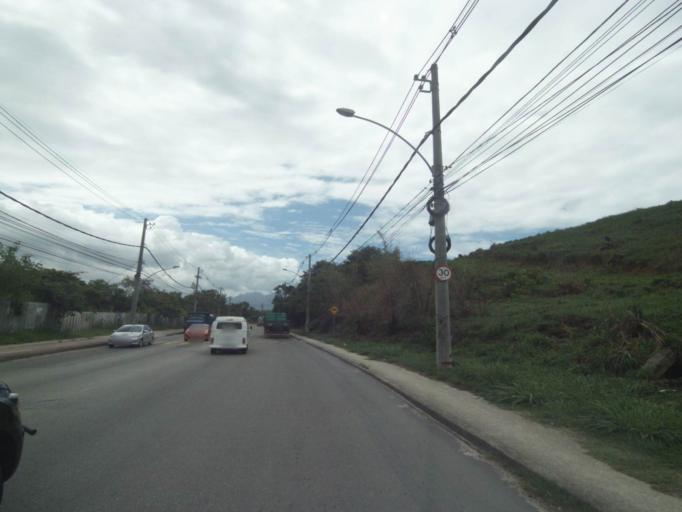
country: BR
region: Rio de Janeiro
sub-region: Nilopolis
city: Nilopolis
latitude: -22.9851
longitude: -43.4270
